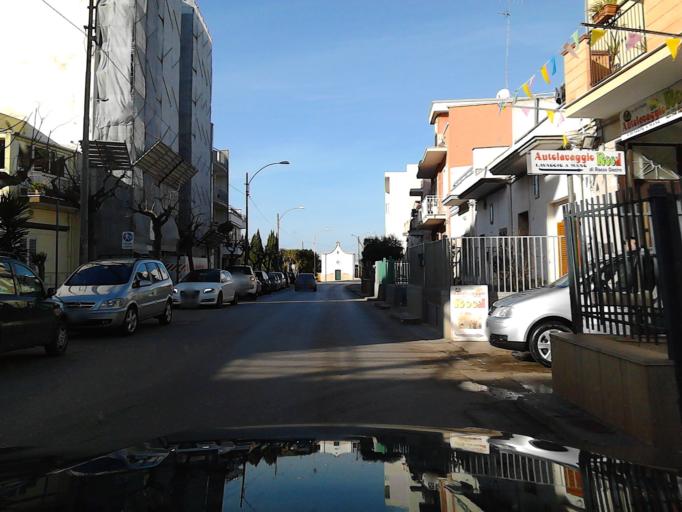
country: IT
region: Apulia
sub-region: Provincia di Bari
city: Rutigliano
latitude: 41.0164
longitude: 17.0001
